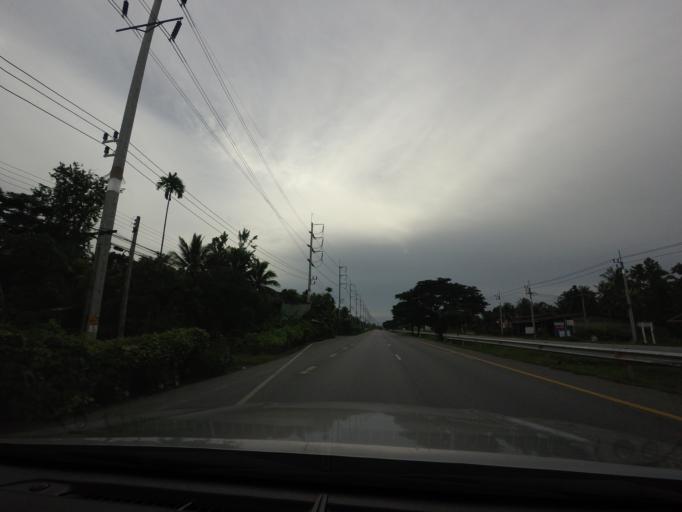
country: TH
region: Nakhon Si Thammarat
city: Chian Yai
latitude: 8.0829
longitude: 100.1635
